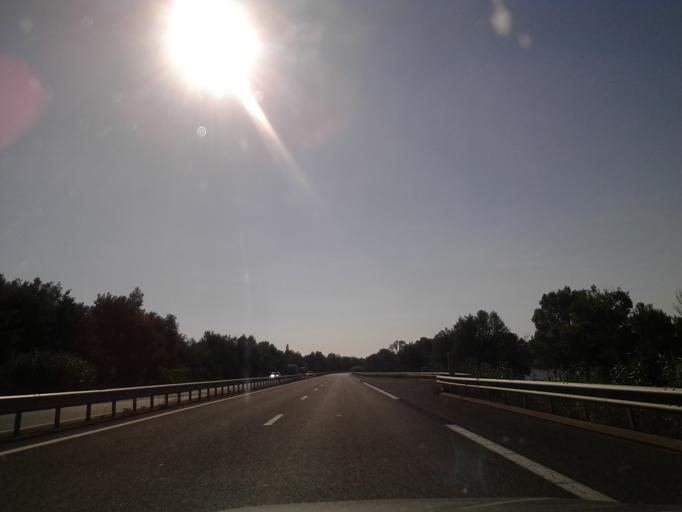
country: FR
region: Languedoc-Roussillon
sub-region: Departement des Pyrenees-Orientales
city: Millas
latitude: 42.6986
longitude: 2.6833
